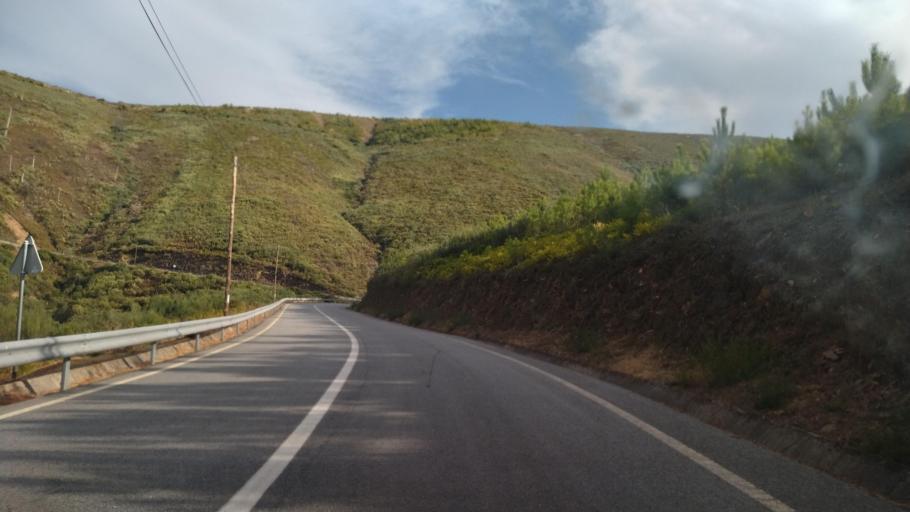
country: PT
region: Castelo Branco
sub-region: Covilha
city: Teixoso
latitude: 40.3698
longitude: -7.4510
